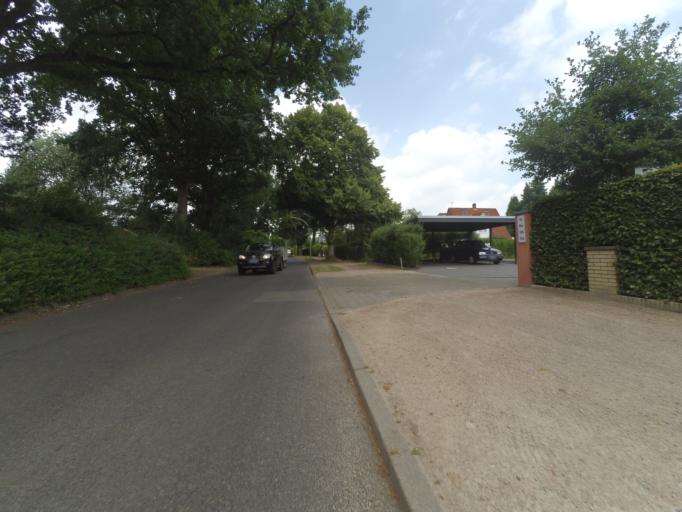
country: DE
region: Hamburg
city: Sasel
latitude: 53.6408
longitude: 10.1231
